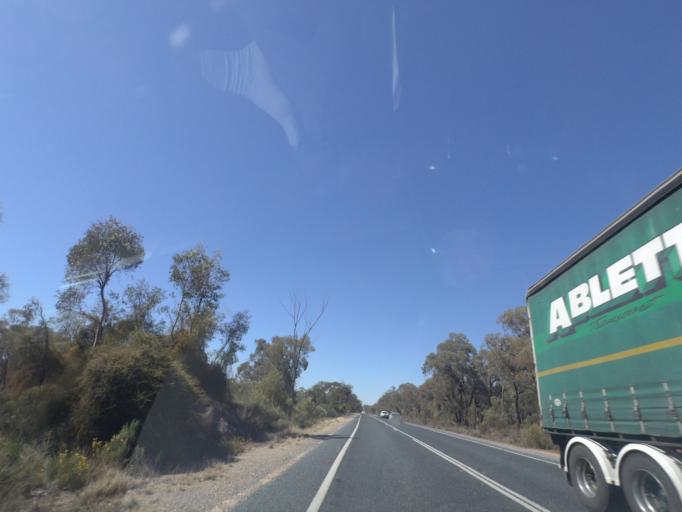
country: AU
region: New South Wales
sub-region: Bland
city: West Wyalong
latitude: -34.1401
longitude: 147.1203
